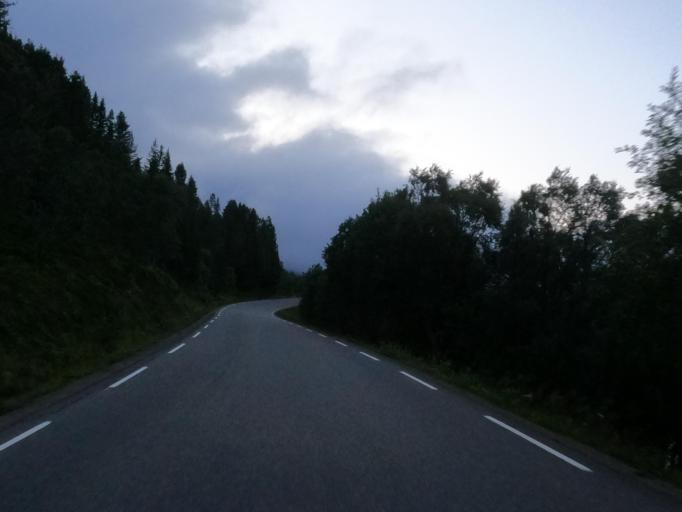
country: NO
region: Nordland
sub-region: Lodingen
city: Lodingen
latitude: 68.5988
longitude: 15.7888
